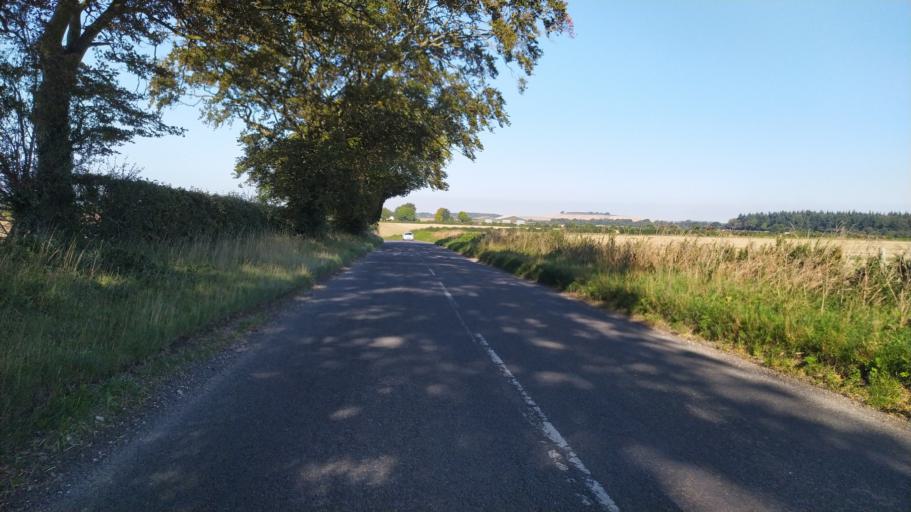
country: GB
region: England
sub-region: Hampshire
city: Abbotts Ann
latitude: 51.1614
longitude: -1.5713
